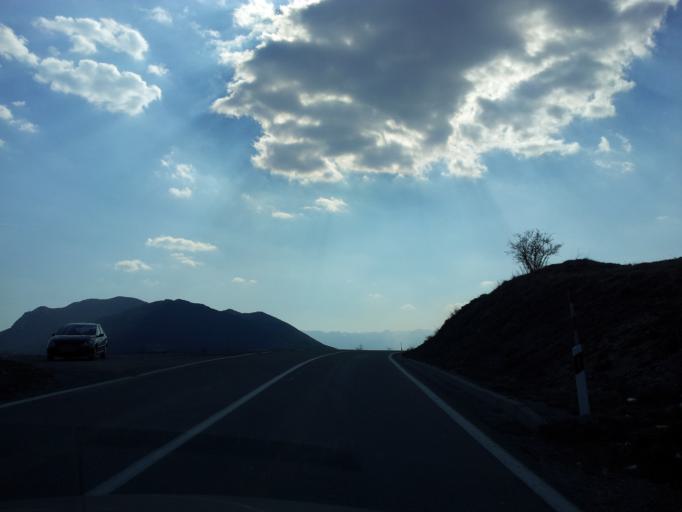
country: HR
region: Zadarska
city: Gracac
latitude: 44.5360
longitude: 15.7452
